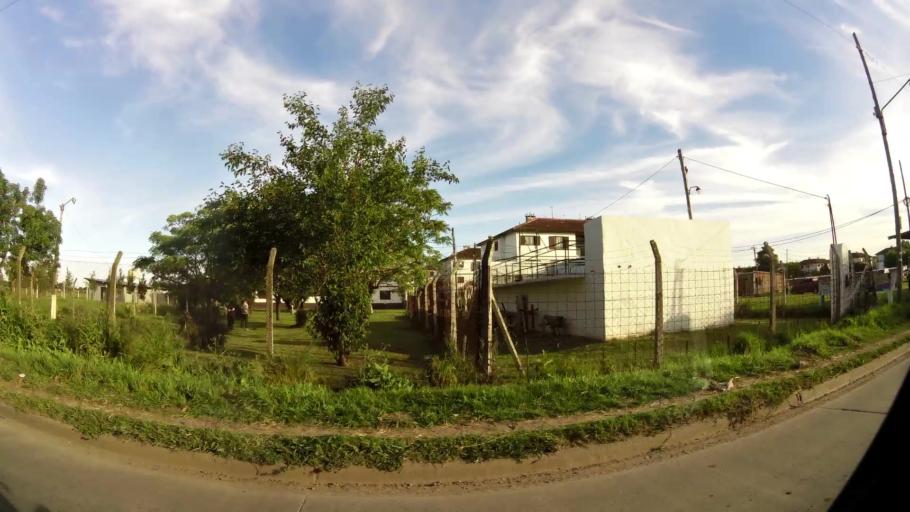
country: AR
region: Buenos Aires
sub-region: Partido de Almirante Brown
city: Adrogue
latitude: -34.8200
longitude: -58.3392
